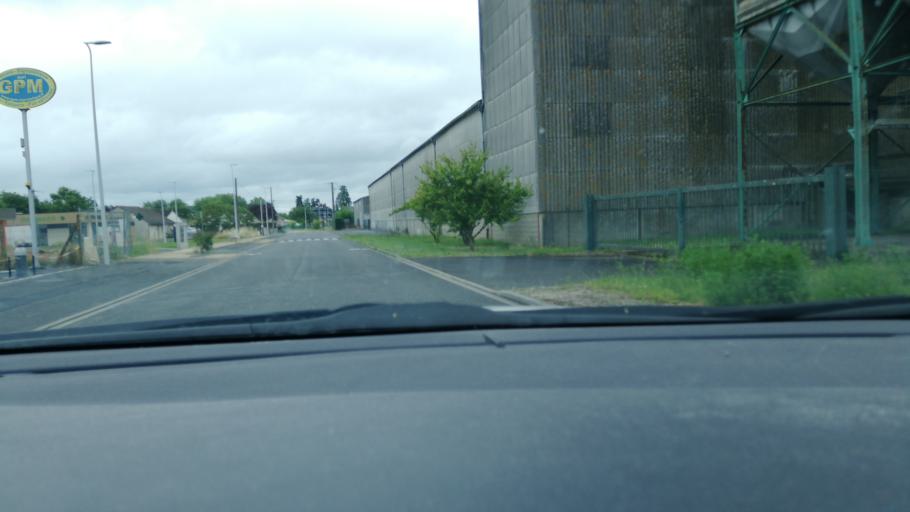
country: FR
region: Poitou-Charentes
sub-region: Departement de la Vienne
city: Antran
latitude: 46.8717
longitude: 0.5658
